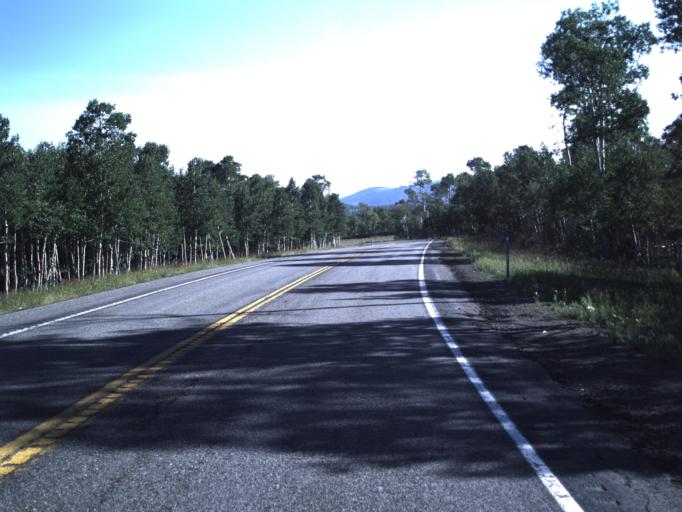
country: US
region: Utah
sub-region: Sanpete County
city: Fairview
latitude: 39.6563
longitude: -111.3298
